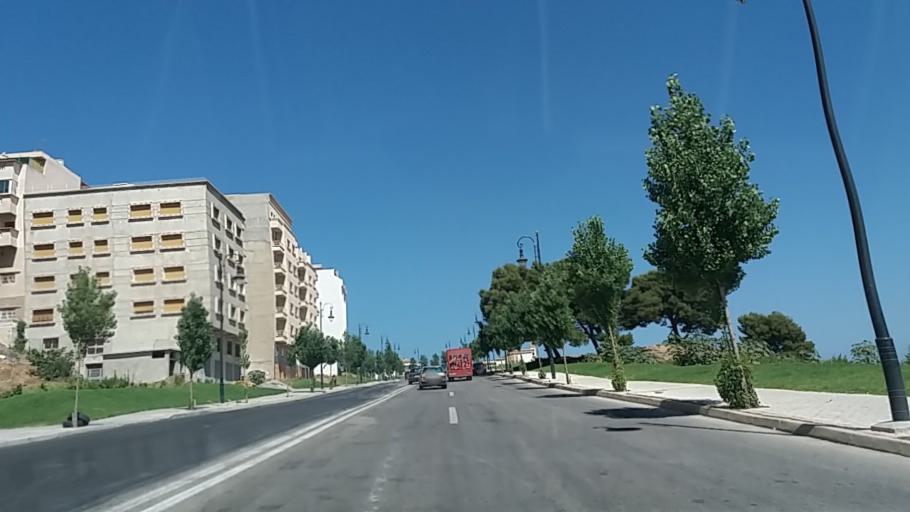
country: MA
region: Tanger-Tetouan
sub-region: Tanger-Assilah
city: Tangier
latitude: 35.7698
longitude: -5.7635
